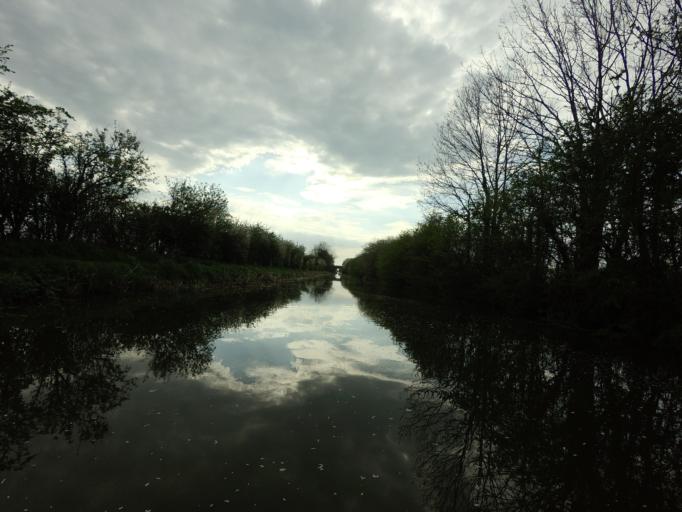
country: GB
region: England
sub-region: Buckinghamshire
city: Aston Clinton
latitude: 51.8202
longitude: -0.6947
